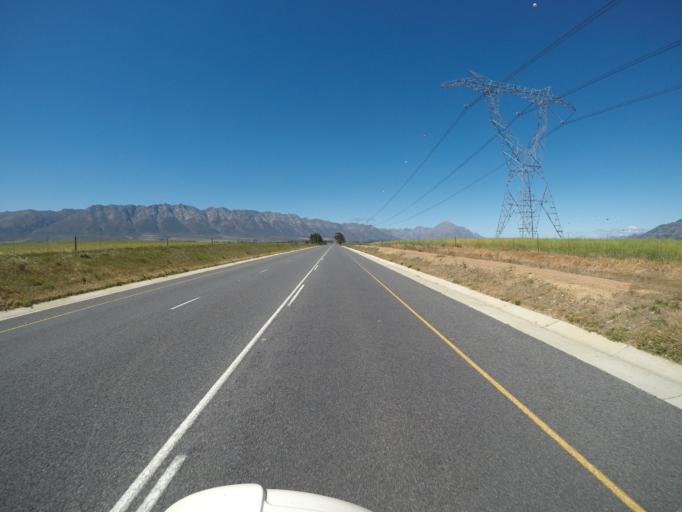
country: ZA
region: Western Cape
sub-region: Cape Winelands District Municipality
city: Ceres
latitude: -33.3169
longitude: 19.1316
